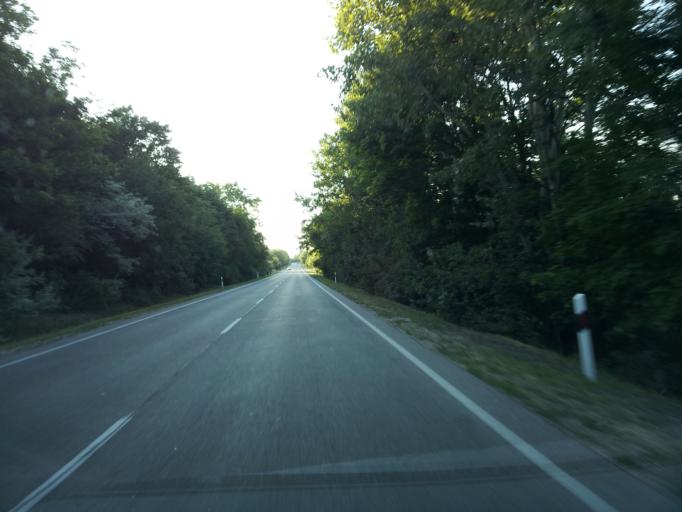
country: HU
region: Fejer
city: Szarliget
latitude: 47.5239
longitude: 18.4692
